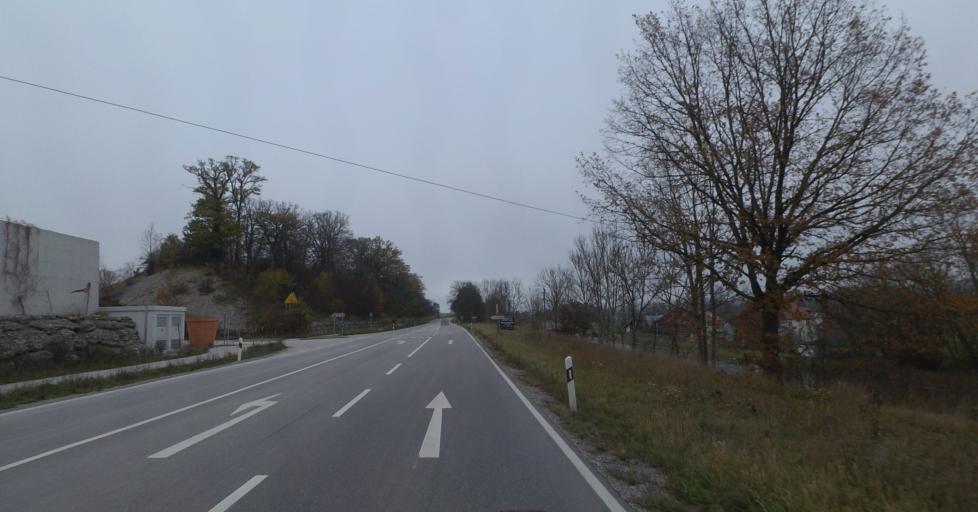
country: DE
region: Bavaria
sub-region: Upper Bavaria
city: Trostberg an der Alz
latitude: 48.0461
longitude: 12.5645
